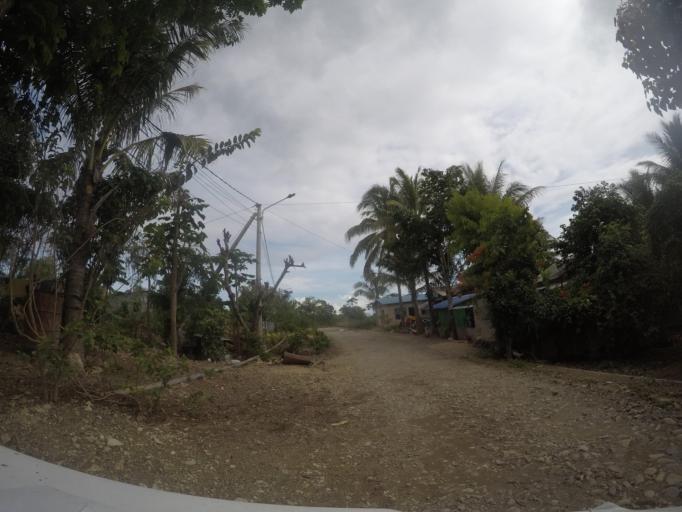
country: TL
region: Baucau
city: Baucau
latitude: -8.4760
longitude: 126.4537
